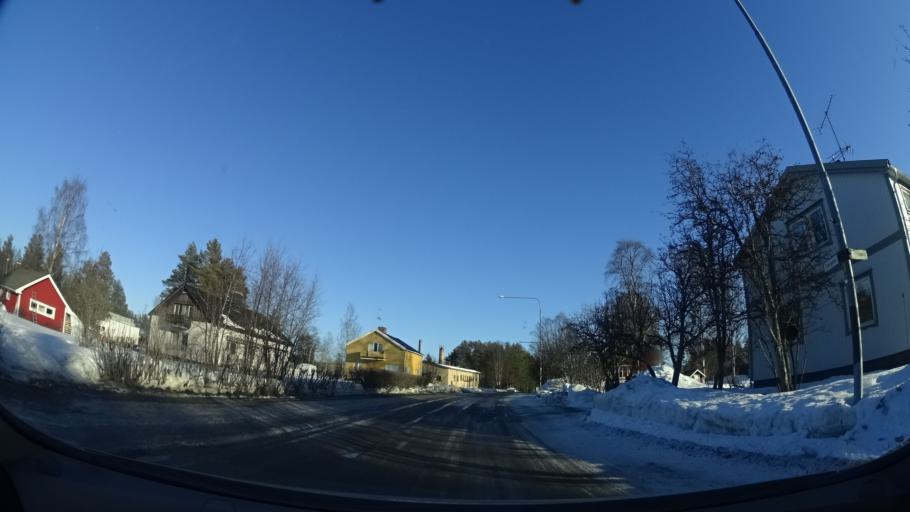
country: SE
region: Vaesterbotten
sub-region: Skelleftea Kommun
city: Langsele
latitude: 65.0583
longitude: 20.0435
